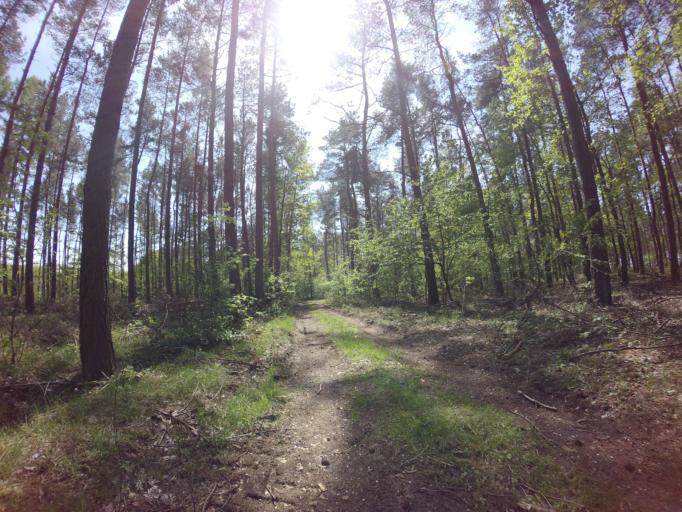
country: PL
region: West Pomeranian Voivodeship
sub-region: Powiat choszczenski
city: Choszczno
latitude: 53.1659
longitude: 15.3803
